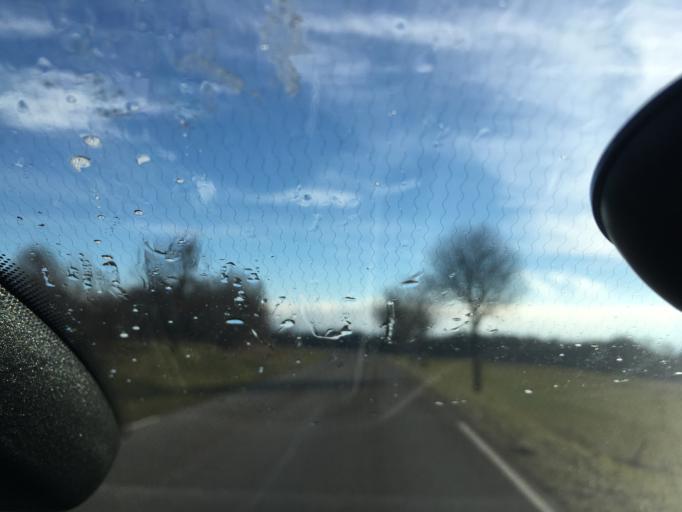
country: DE
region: Baden-Wuerttemberg
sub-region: Freiburg Region
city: Gorwihl
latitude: 47.6365
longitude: 8.0826
